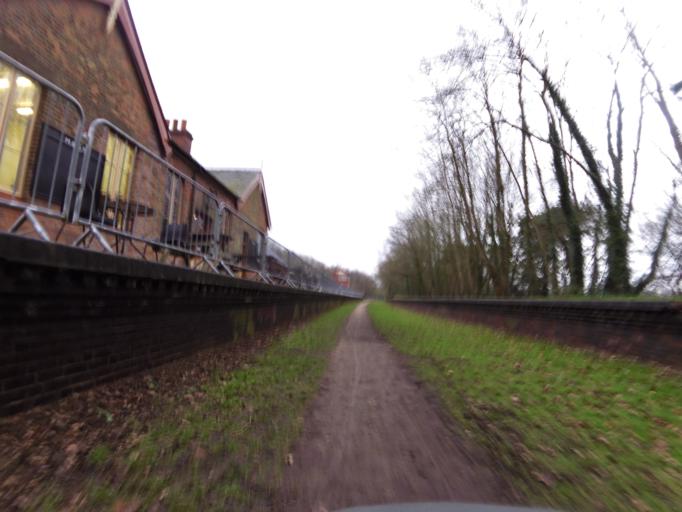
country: GB
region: England
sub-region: Norfolk
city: Briston
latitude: 52.7519
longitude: 1.0975
